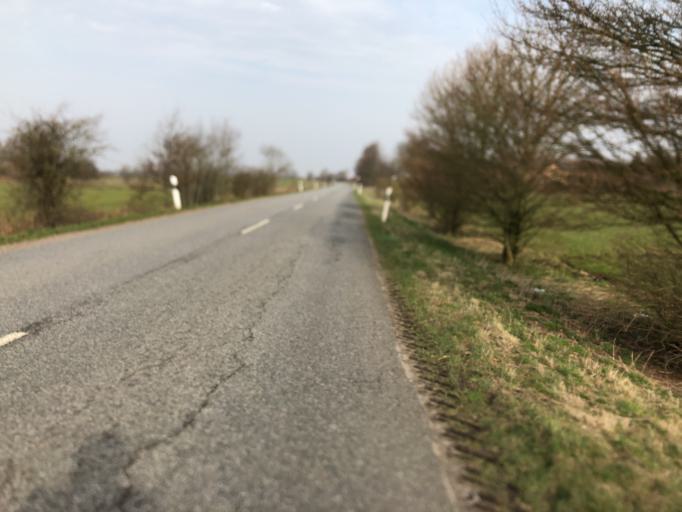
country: DE
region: Schleswig-Holstein
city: Sankelmark
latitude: 54.7047
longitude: 9.3906
